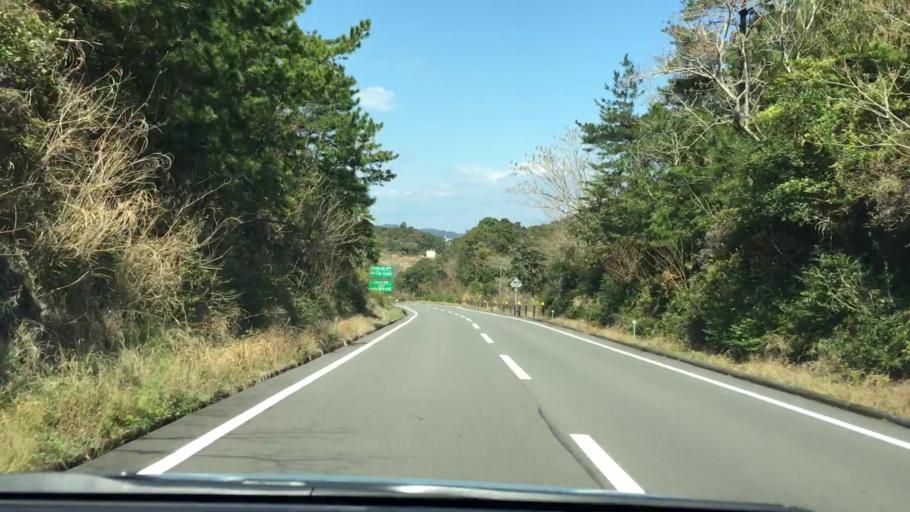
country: JP
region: Mie
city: Toba
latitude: 34.4359
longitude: 136.9123
